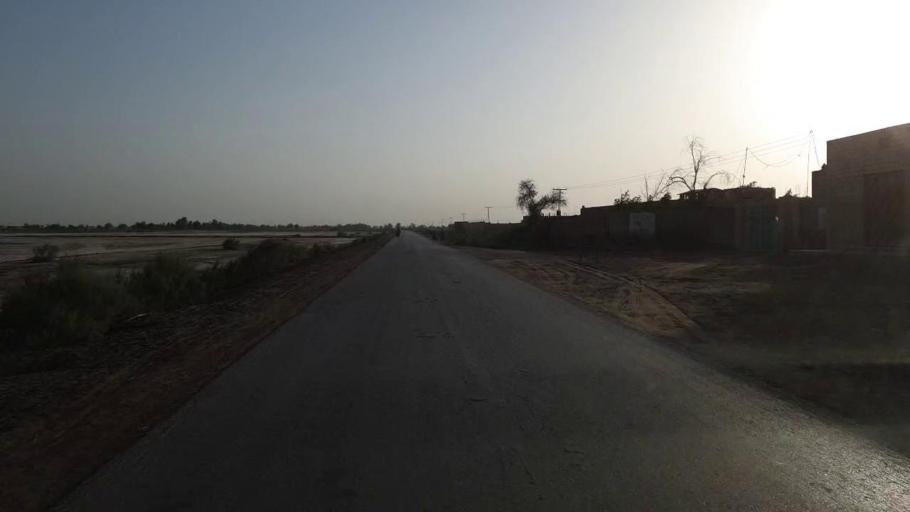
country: PK
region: Sindh
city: Jam Sahib
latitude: 26.2899
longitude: 68.6080
